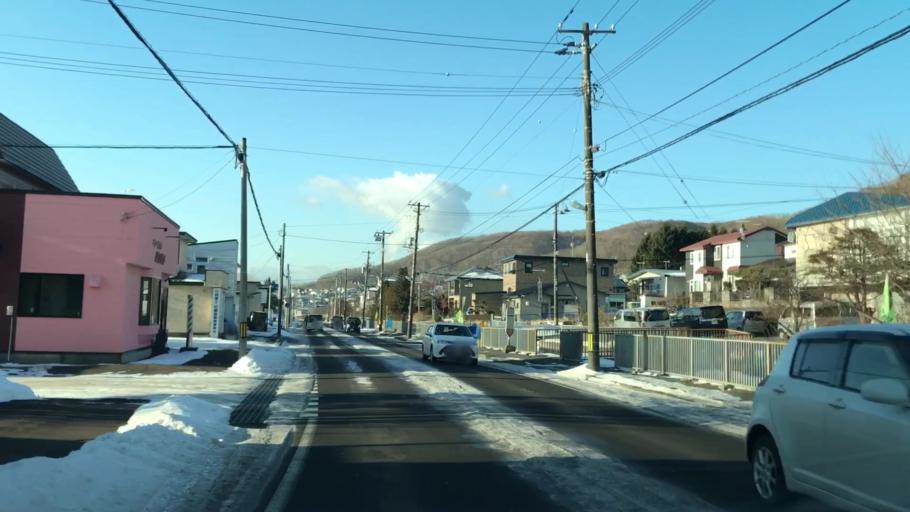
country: JP
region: Hokkaido
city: Muroran
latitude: 42.3738
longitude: 141.0572
